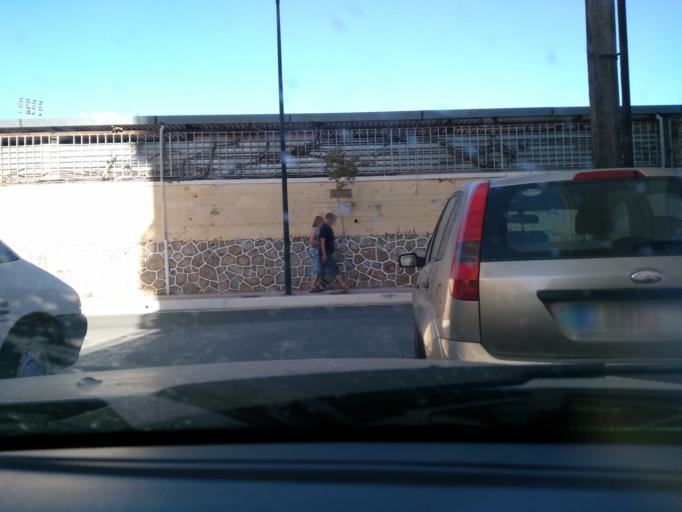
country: GR
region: Crete
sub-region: Nomos Lasithiou
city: Agios Nikolaos
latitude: 35.1866
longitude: 25.7138
